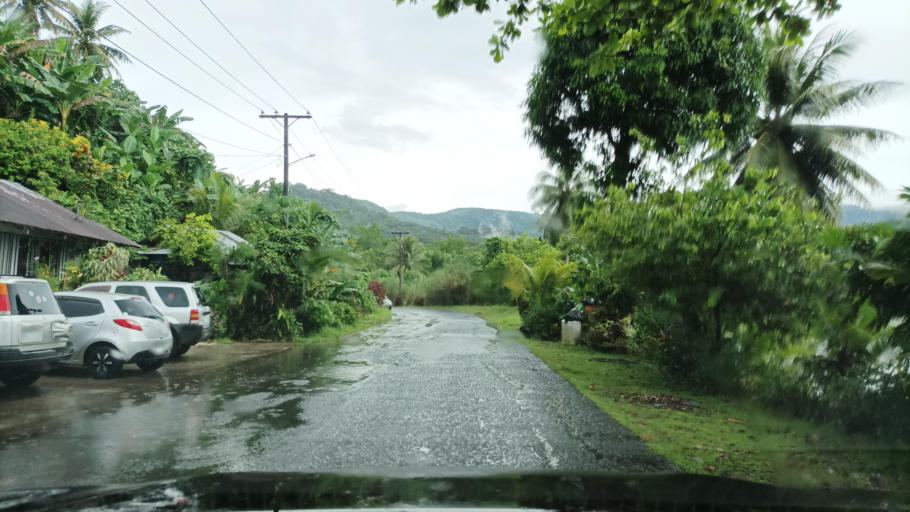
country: FM
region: Pohnpei
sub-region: Kolonia Municipality
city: Kolonia
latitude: 6.9527
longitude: 158.2301
